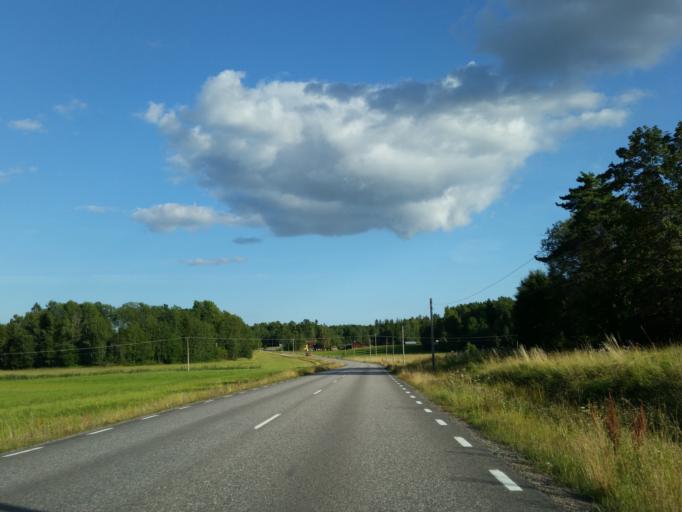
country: SE
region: Stockholm
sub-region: Sodertalje Kommun
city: Molnbo
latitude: 58.9964
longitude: 17.4094
